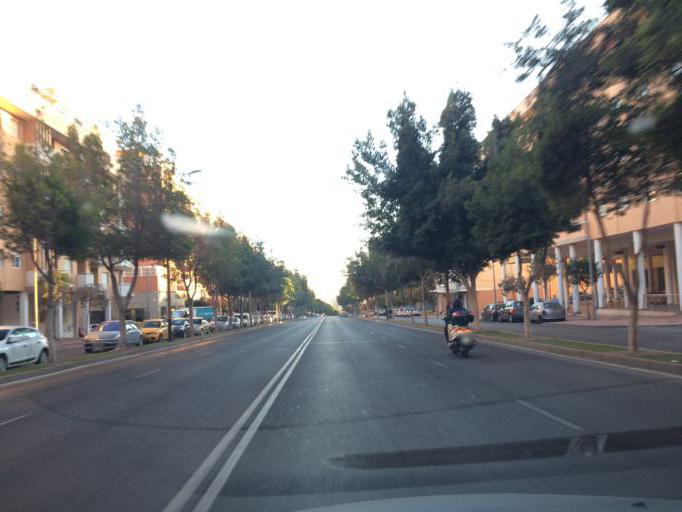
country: ES
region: Andalusia
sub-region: Provincia de Almeria
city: Almeria
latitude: 36.8508
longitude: -2.4465
